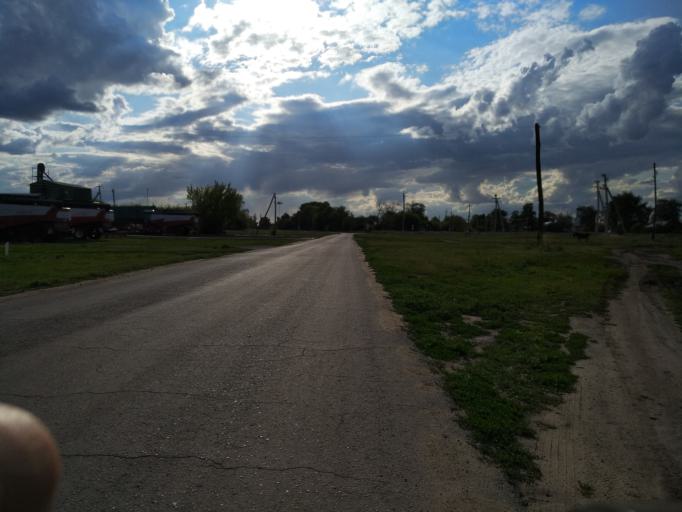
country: RU
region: Lipetsk
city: Dobrinka
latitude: 52.0385
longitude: 40.5429
